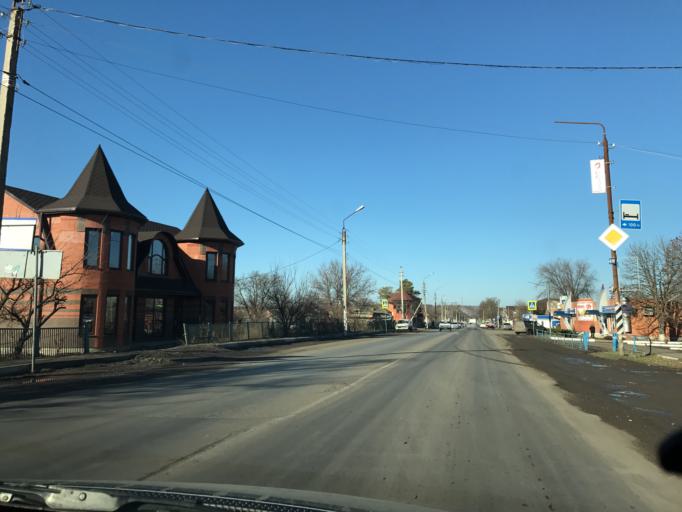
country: RU
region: Rostov
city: Kagal'nitskaya
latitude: 46.8788
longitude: 40.1544
